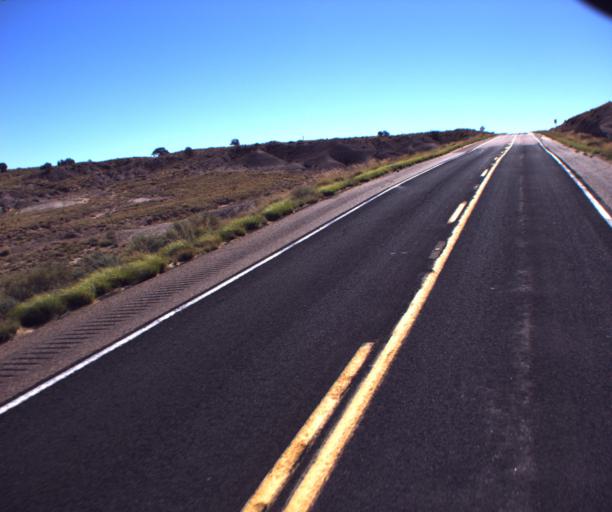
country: US
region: Arizona
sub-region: Navajo County
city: Snowflake
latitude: 34.7179
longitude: -109.7699
